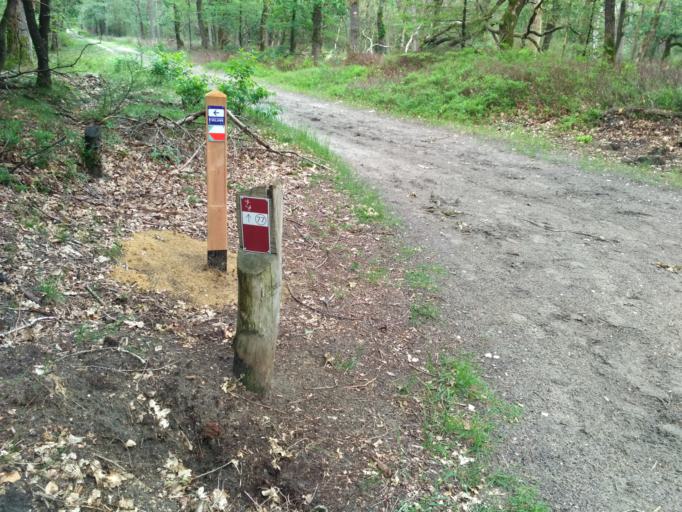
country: NL
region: Gelderland
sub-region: Gemeente Apeldoorn
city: Beekbergen
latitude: 52.1428
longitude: 5.9033
